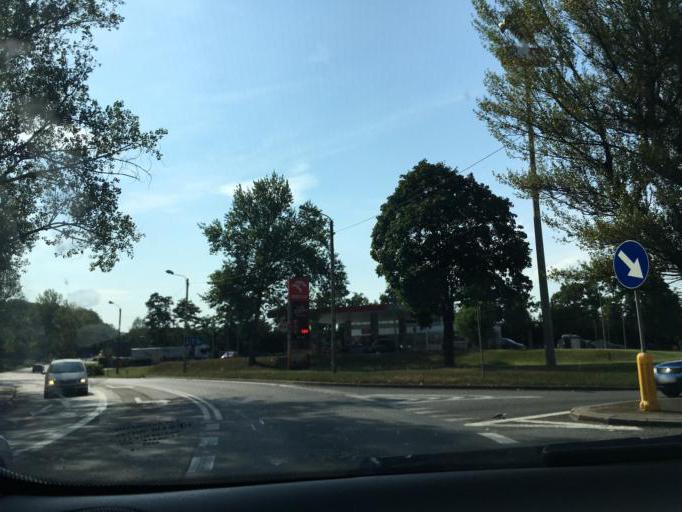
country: PL
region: Opole Voivodeship
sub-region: Powiat nyski
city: Nysa
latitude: 50.4819
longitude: 17.3134
